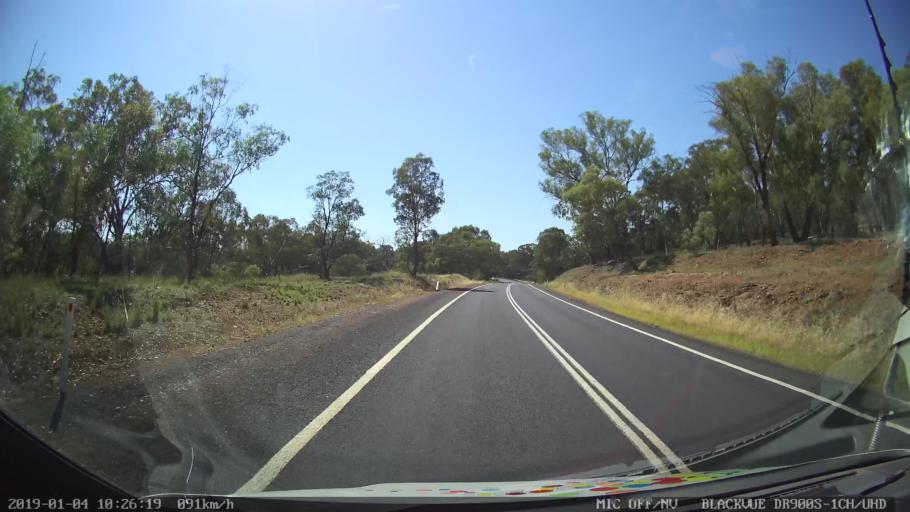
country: AU
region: New South Wales
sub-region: Cabonne
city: Canowindra
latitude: -33.3731
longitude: 148.5835
